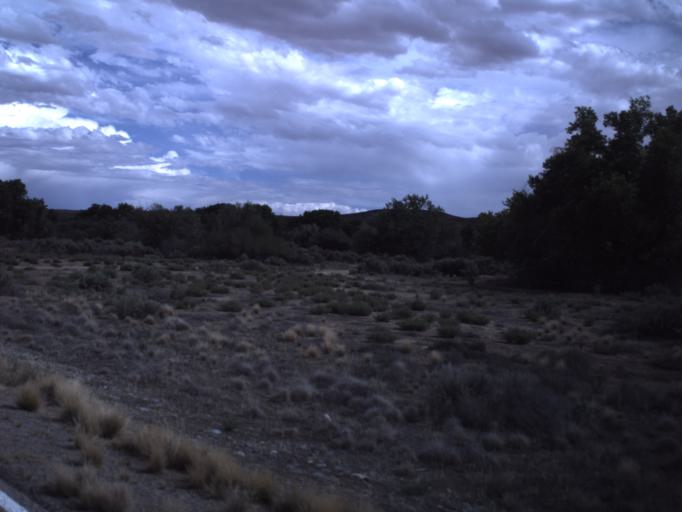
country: US
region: Utah
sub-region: San Juan County
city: Blanding
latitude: 37.2820
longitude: -109.5097
